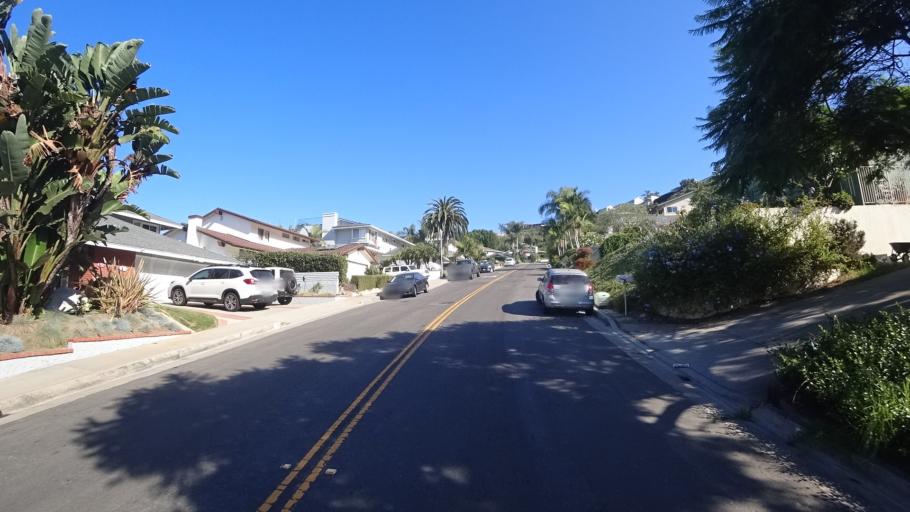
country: US
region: California
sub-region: Orange County
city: San Clemente
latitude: 33.4231
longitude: -117.6020
